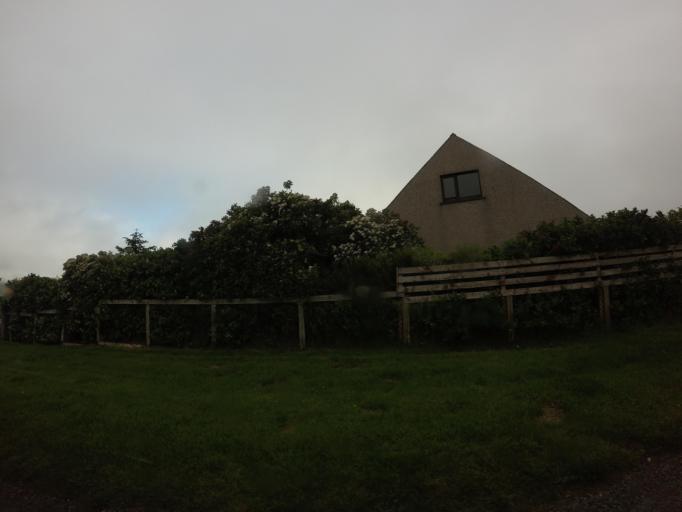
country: GB
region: Scotland
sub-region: Eilean Siar
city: Stornoway
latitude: 58.1949
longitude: -6.2228
